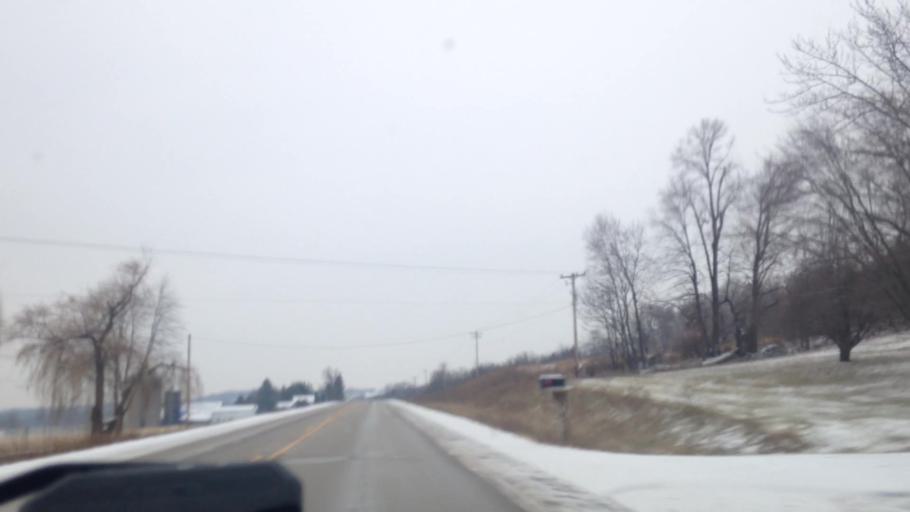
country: US
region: Wisconsin
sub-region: Dodge County
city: Hustisford
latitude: 43.2909
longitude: -88.5186
